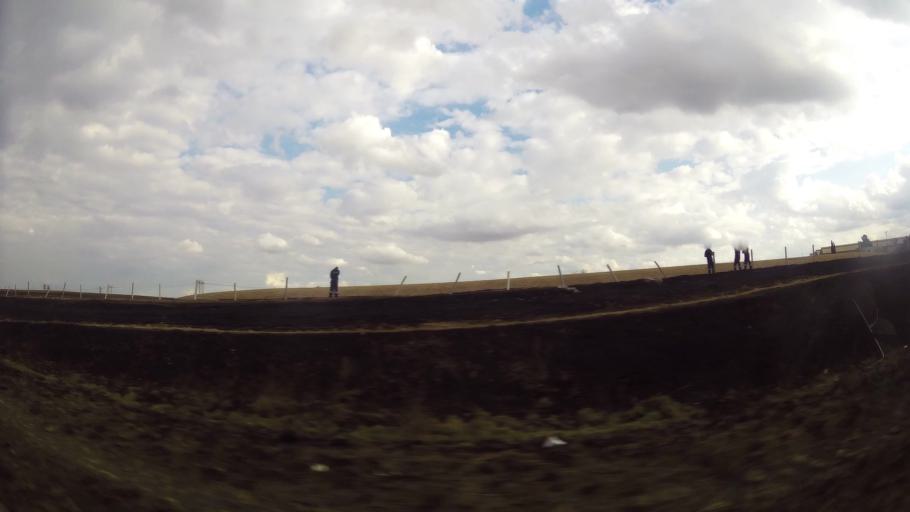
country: ZA
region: Orange Free State
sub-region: Fezile Dabi District Municipality
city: Sasolburg
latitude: -26.8317
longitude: 27.8589
